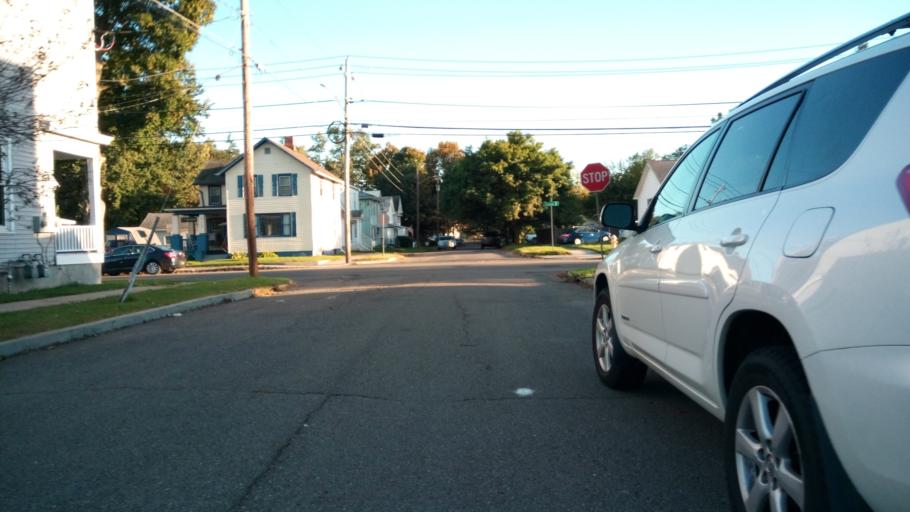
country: US
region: New York
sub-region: Chemung County
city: Elmira
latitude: 42.0828
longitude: -76.8104
